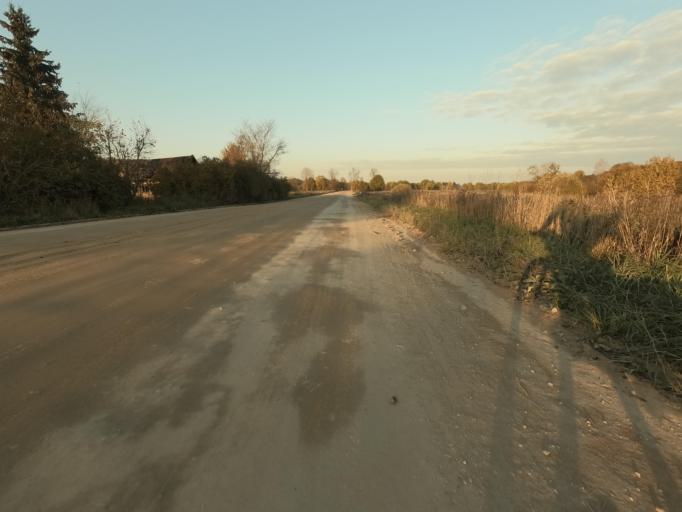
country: RU
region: Leningrad
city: Lyuban'
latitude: 59.0238
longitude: 31.0998
